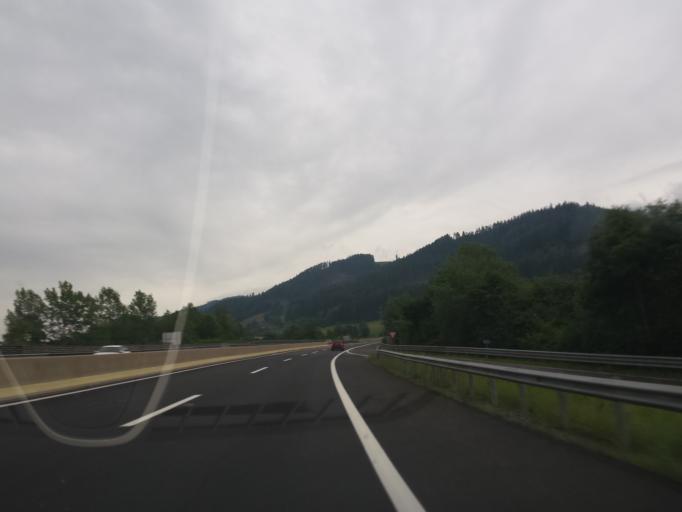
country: AT
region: Styria
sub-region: Politischer Bezirk Bruck-Muerzzuschlag
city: Kindberg
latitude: 47.5111
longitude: 15.4576
